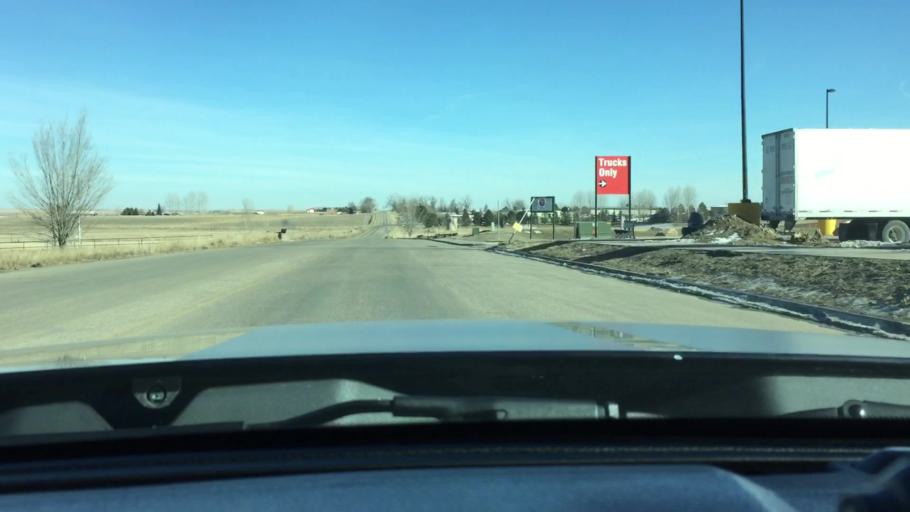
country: US
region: Colorado
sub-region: Weld County
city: Johnstown
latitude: 40.3636
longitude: -104.9822
